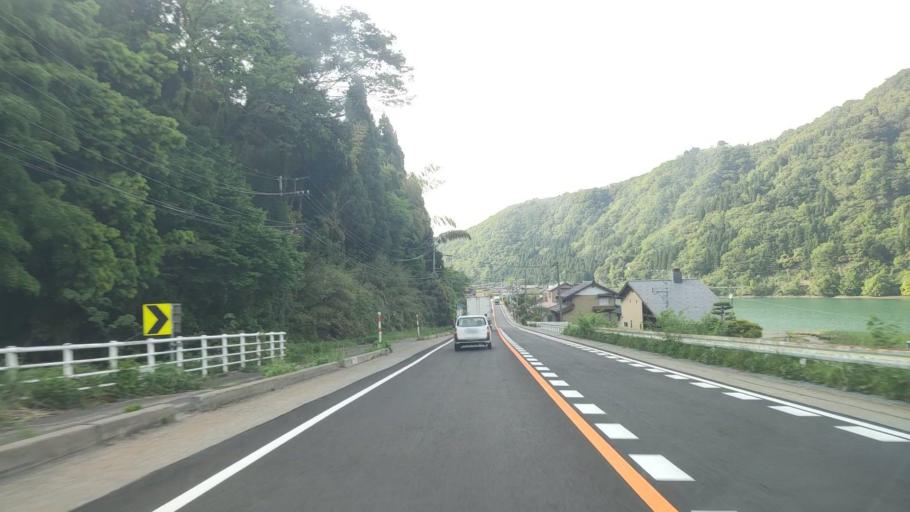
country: JP
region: Toyama
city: Yatsuomachi-higashikumisaka
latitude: 36.5480
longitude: 137.2254
